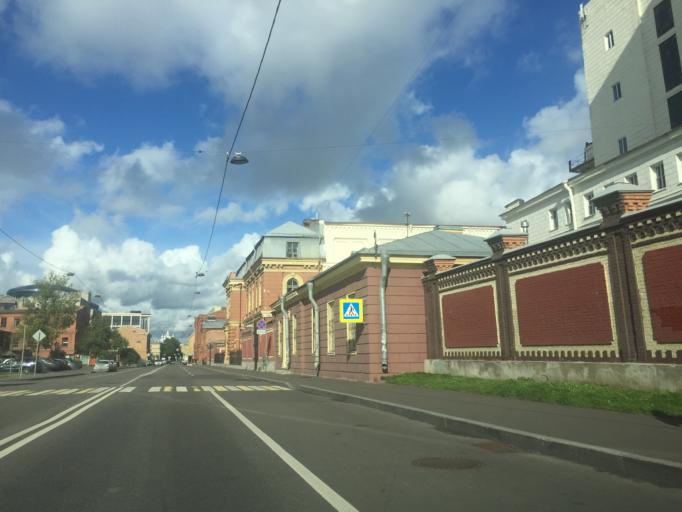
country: RU
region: St.-Petersburg
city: Centralniy
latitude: 59.9346
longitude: 30.3848
